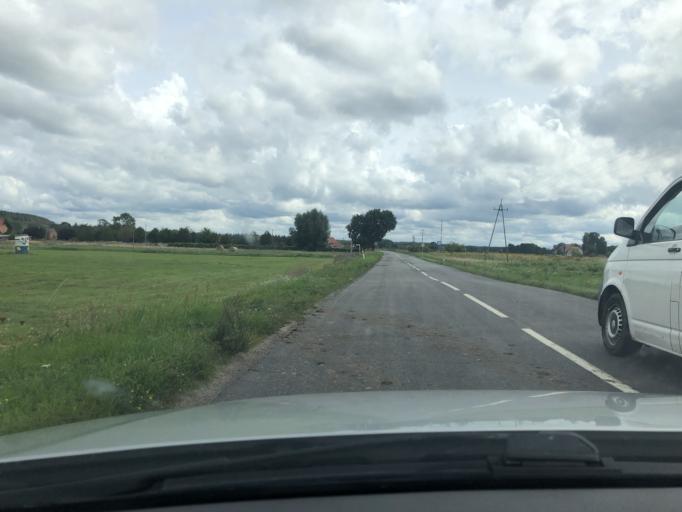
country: PL
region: Lubusz
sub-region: Powiat strzelecko-drezdenecki
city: Drezdenko
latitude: 52.8425
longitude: 15.8974
